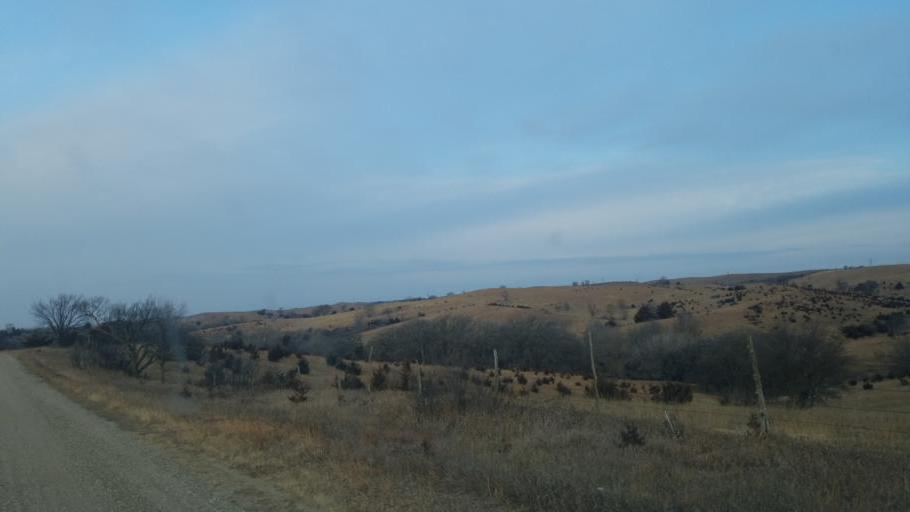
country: US
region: Nebraska
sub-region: Knox County
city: Center
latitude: 42.5609
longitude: -97.7899
